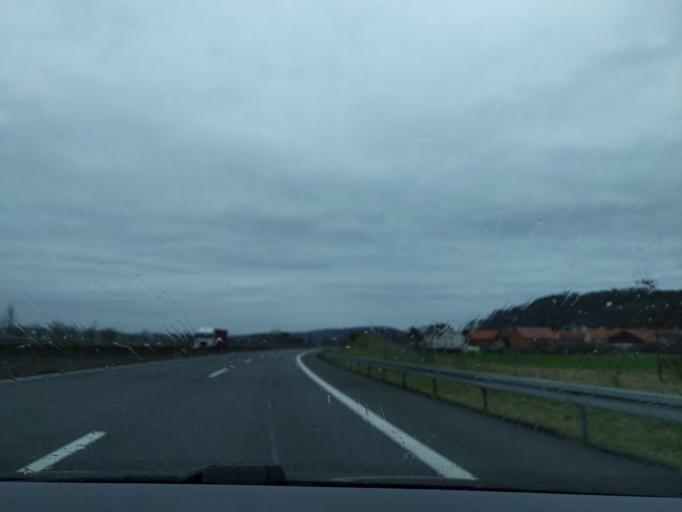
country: DE
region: Hesse
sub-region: Regierungsbezirk Giessen
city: Fronhausen
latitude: 50.7291
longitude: 8.7353
